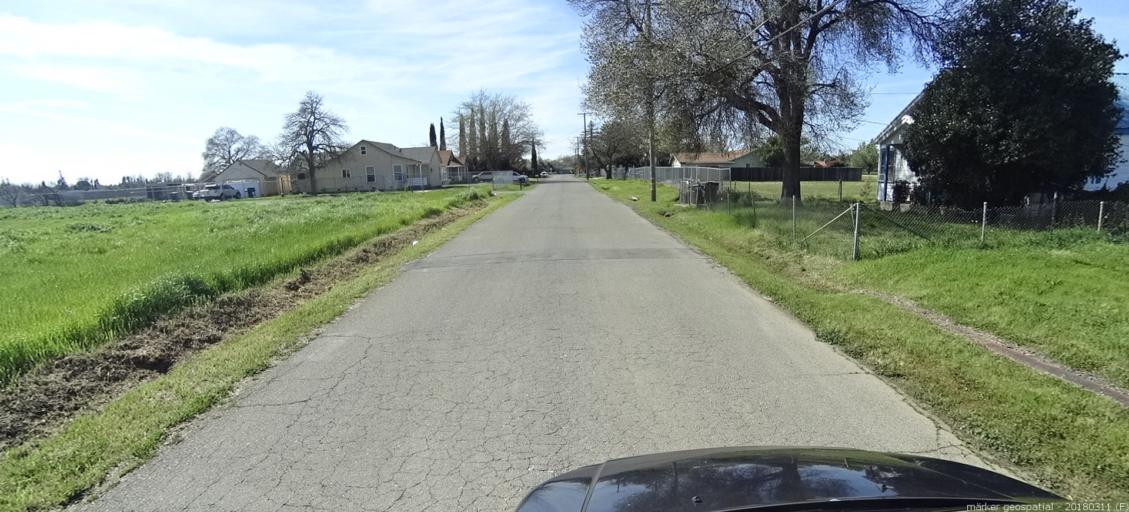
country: US
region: California
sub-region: Sacramento County
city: Florin
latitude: 38.4827
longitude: -121.4241
